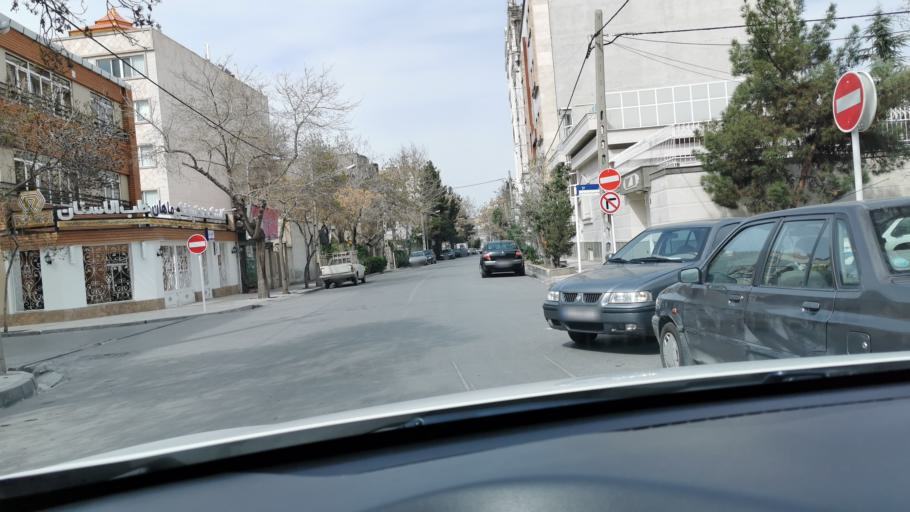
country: IR
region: Razavi Khorasan
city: Mashhad
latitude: 36.2916
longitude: 59.5767
